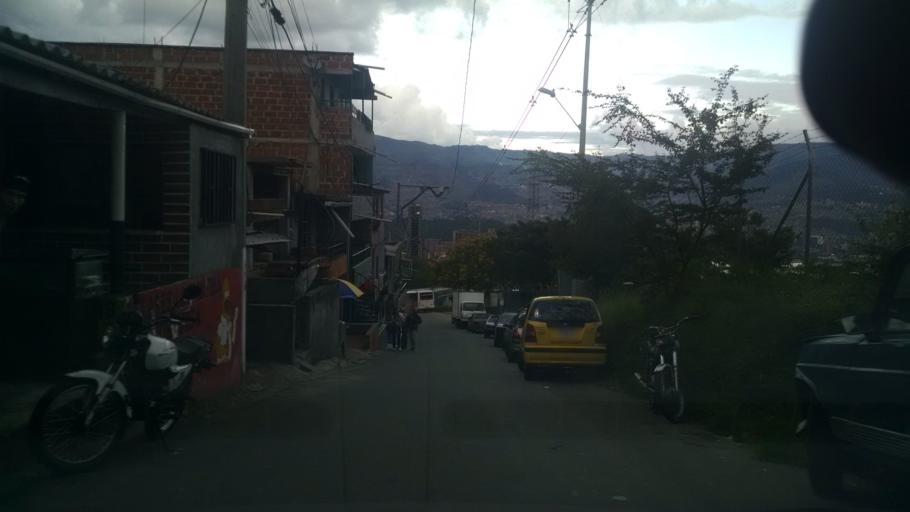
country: CO
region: Antioquia
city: Medellin
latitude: 6.2725
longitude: -75.6097
